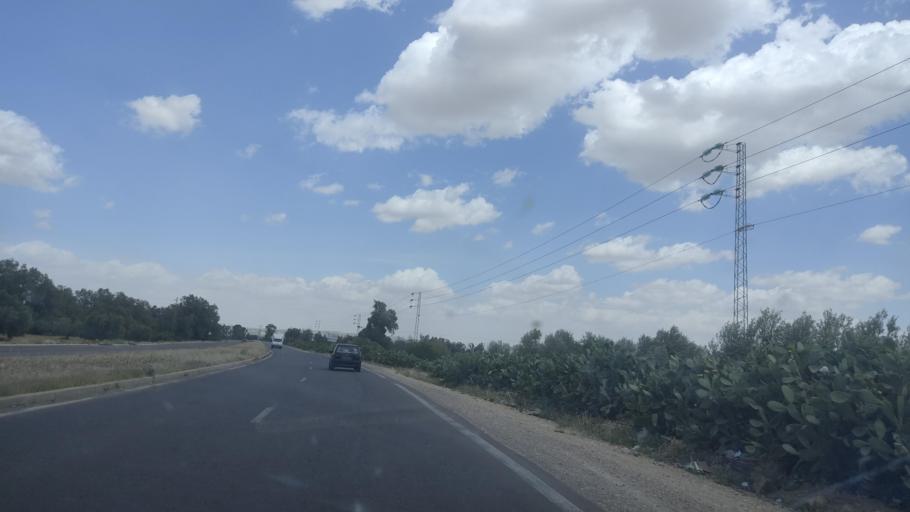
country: TN
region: Al Qasrayn
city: Kasserine
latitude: 35.1973
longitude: 8.8695
